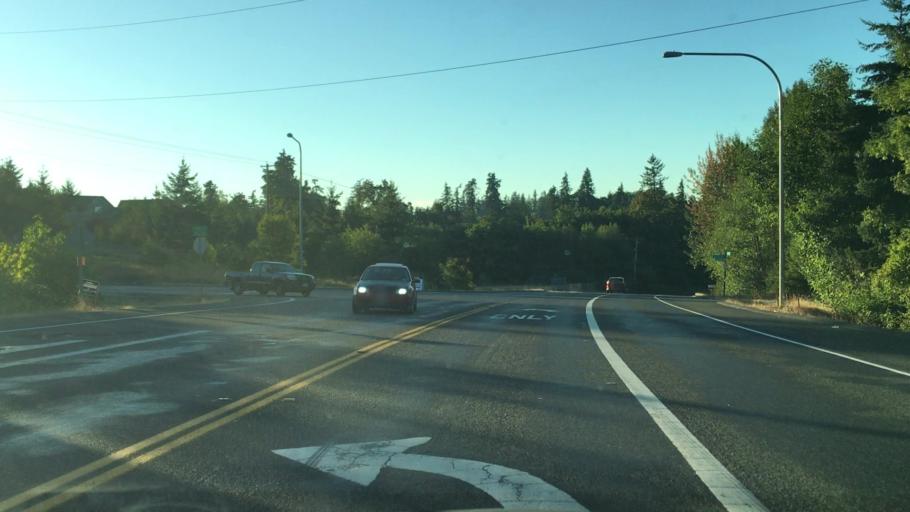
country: US
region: Washington
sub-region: King County
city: Lea Hill
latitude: 47.3310
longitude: -122.1648
